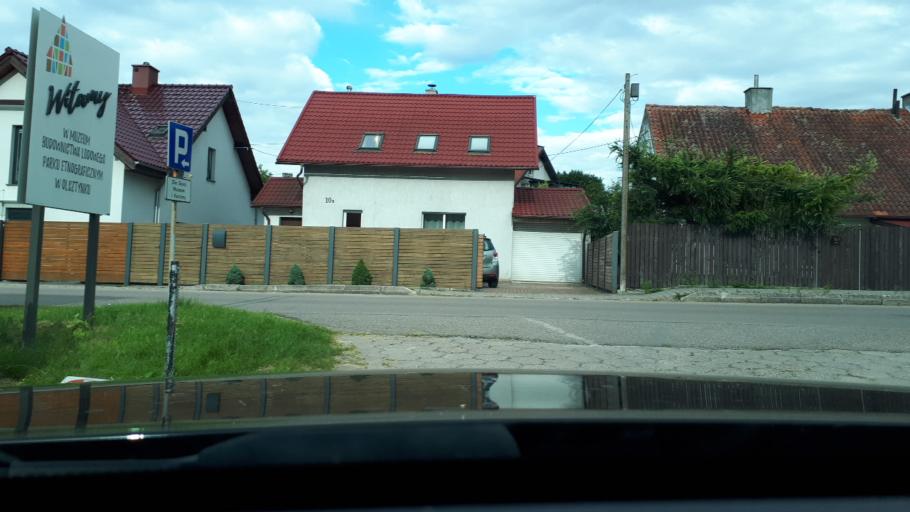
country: PL
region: Warmian-Masurian Voivodeship
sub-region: Powiat olsztynski
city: Olsztynek
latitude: 53.5901
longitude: 20.2896
